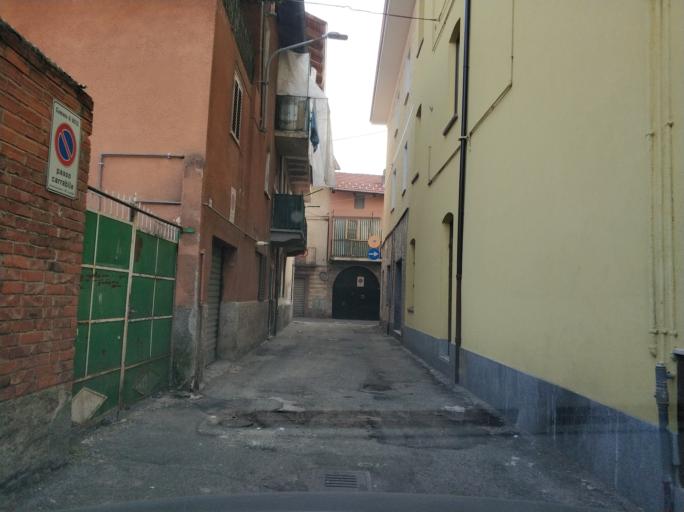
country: IT
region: Piedmont
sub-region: Provincia di Torino
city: Nole
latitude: 45.2448
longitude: 7.5726
